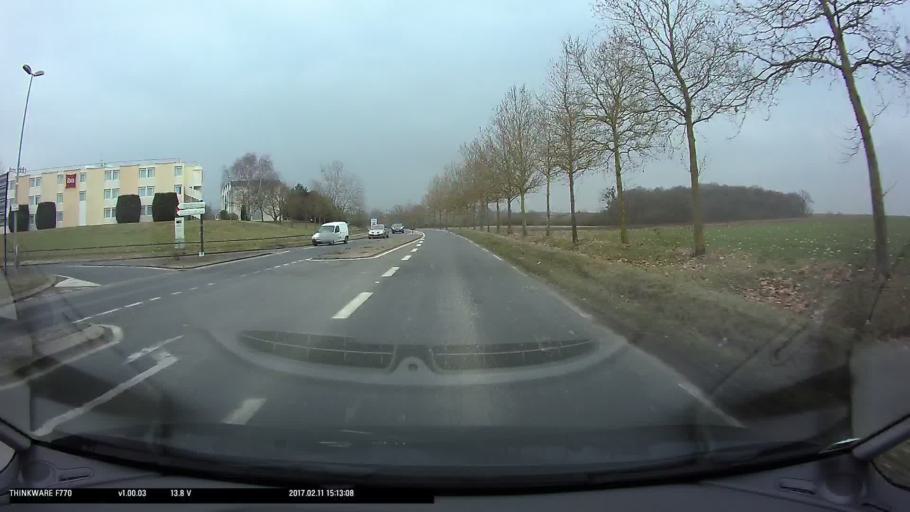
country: FR
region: Ile-de-France
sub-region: Departement des Yvelines
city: Rambouillet
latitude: 48.6217
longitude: 1.8247
